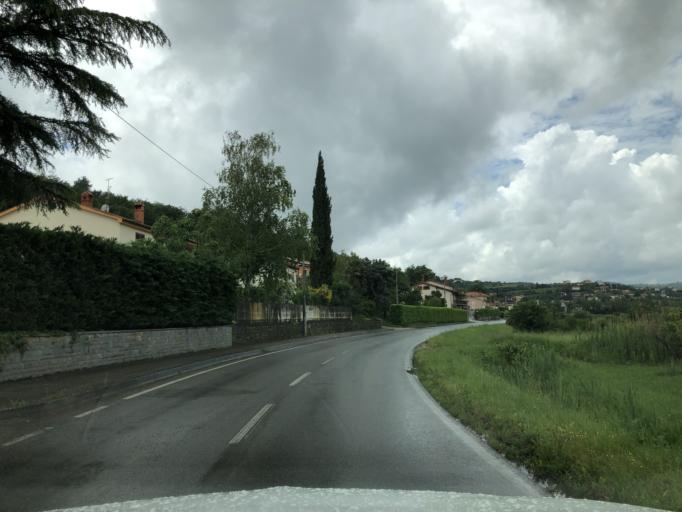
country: SI
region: Koper-Capodistria
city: Prade
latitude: 45.5172
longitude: 13.7733
